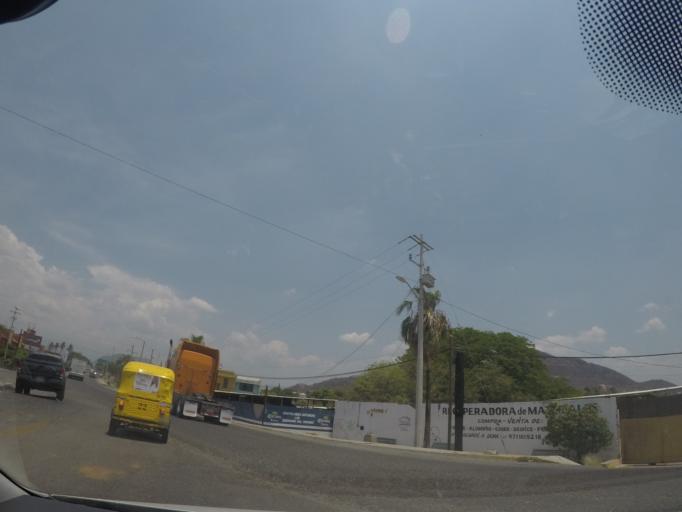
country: MX
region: Oaxaca
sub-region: Santo Domingo Tehuantepec
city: Santo Domingo Tehuantepec
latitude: 16.3245
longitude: -95.2398
